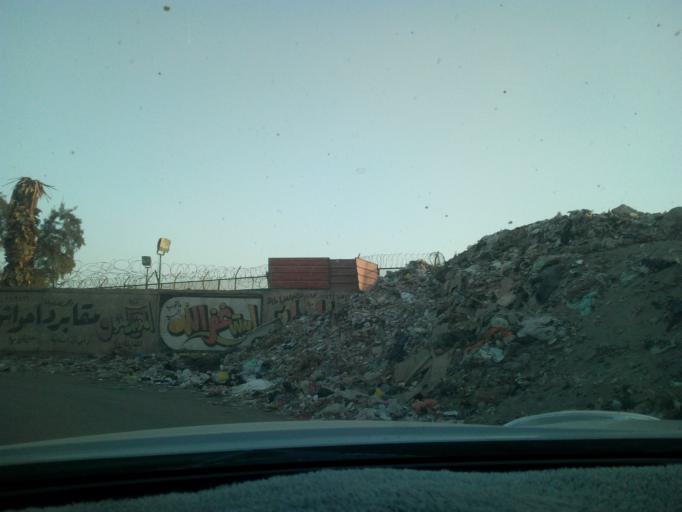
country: EG
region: Muhafazat al Qalyubiyah
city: Al Khankah
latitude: 30.1243
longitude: 31.3561
